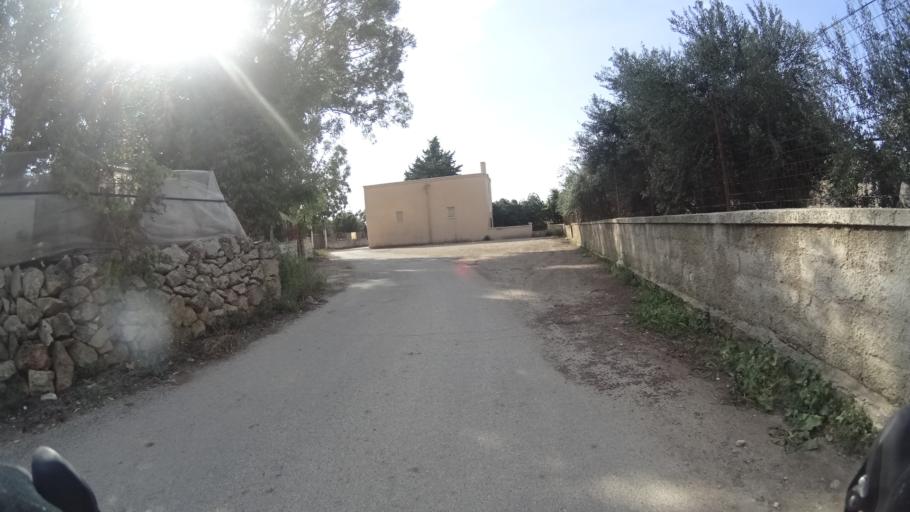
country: IT
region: Apulia
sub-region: Provincia di Taranto
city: Grottaglie
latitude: 40.5138
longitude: 17.4316
